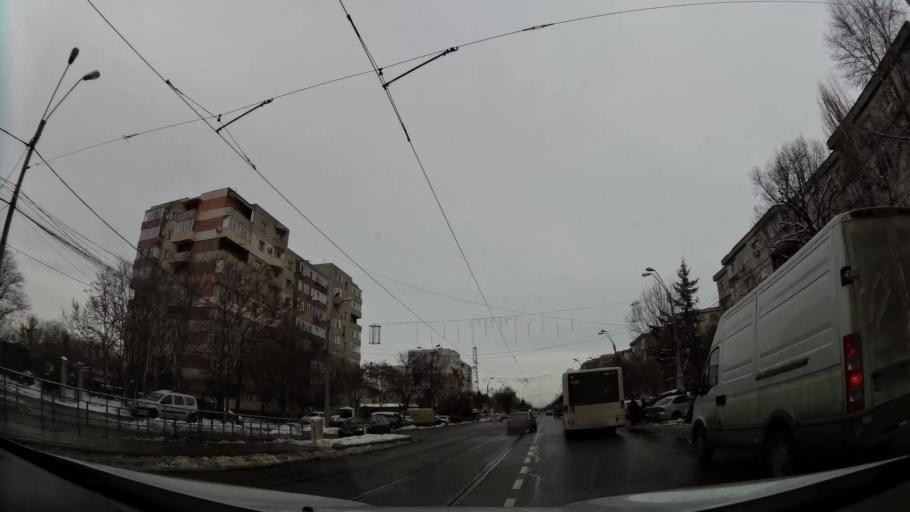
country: RO
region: Ilfov
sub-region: Comuna Popesti-Leordeni
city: Popesti-Leordeni
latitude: 44.3887
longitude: 26.1333
